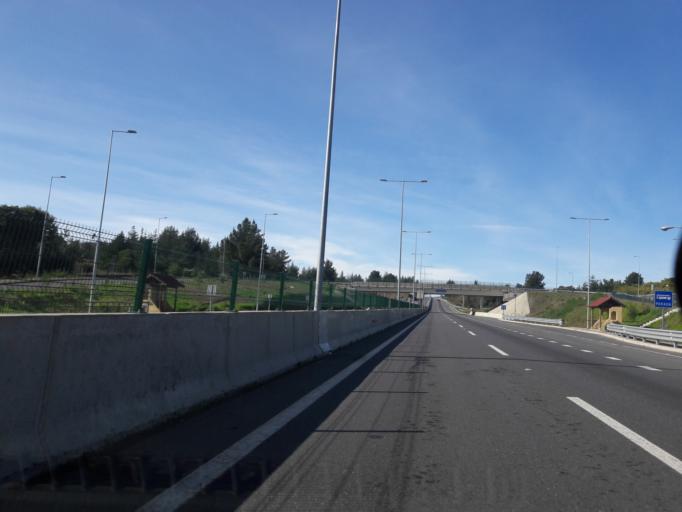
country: CL
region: Biobio
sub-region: Provincia de Biobio
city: Yumbel
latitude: -36.9614
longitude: -72.7218
